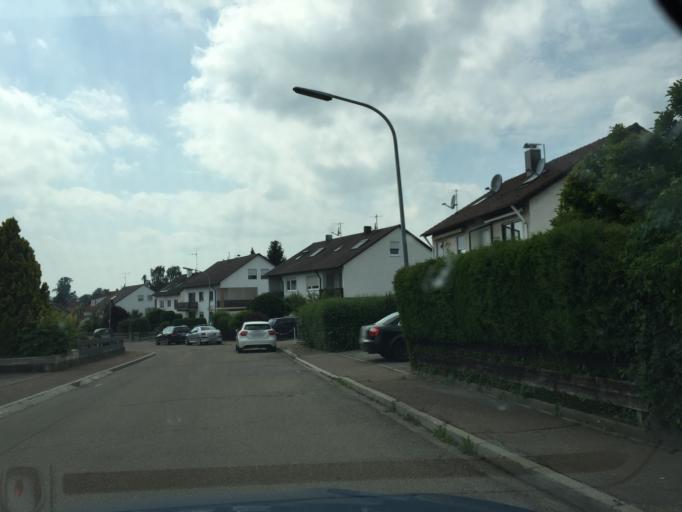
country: DE
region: Bavaria
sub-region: Swabia
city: Senden
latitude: 48.3283
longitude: 10.0599
